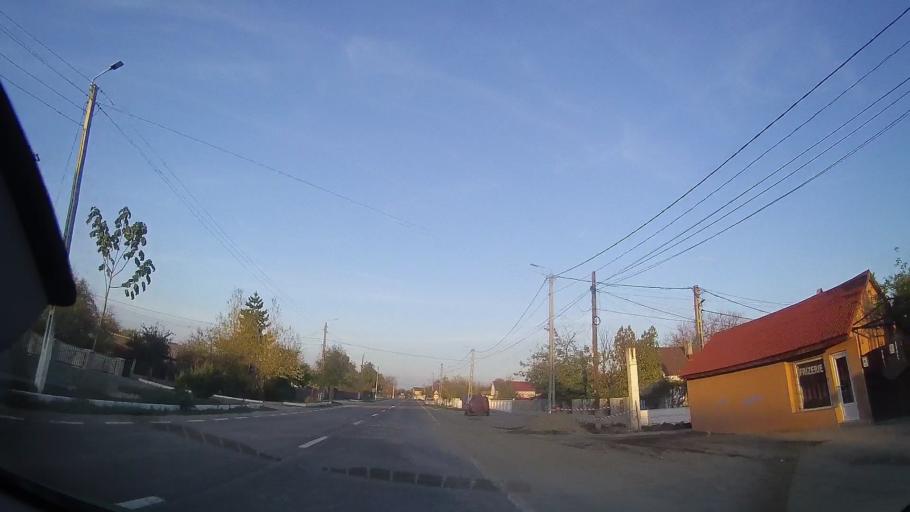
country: RO
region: Constanta
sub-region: Comuna Amzacea
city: Amzacea
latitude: 43.9615
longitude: 28.3962
